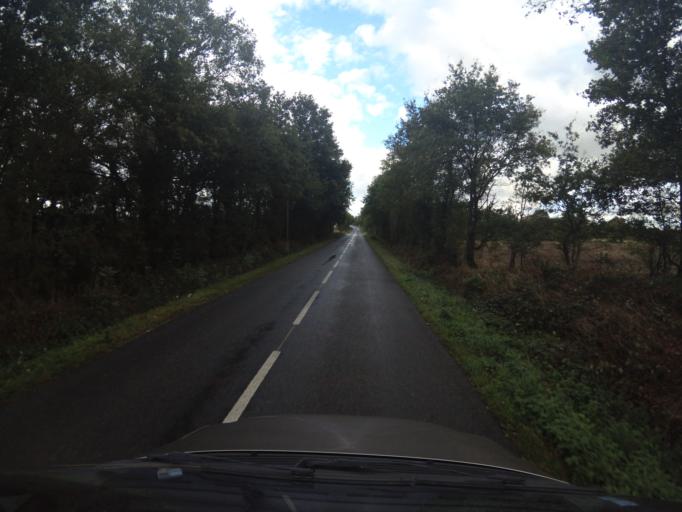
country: FR
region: Pays de la Loire
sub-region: Departement de la Loire-Atlantique
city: Saint-Hilaire-de-Clisson
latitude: 47.0662
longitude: -1.3157
